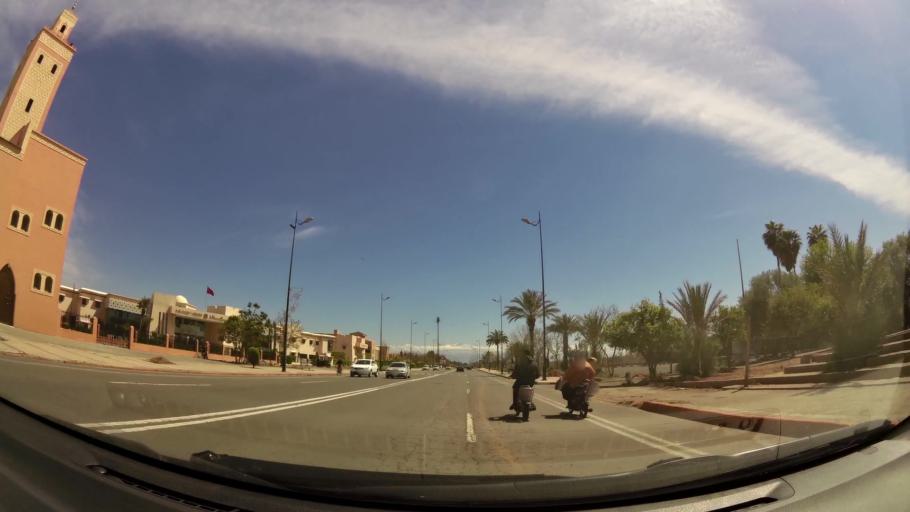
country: MA
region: Marrakech-Tensift-Al Haouz
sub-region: Marrakech
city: Marrakesh
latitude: 31.6124
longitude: -7.9747
